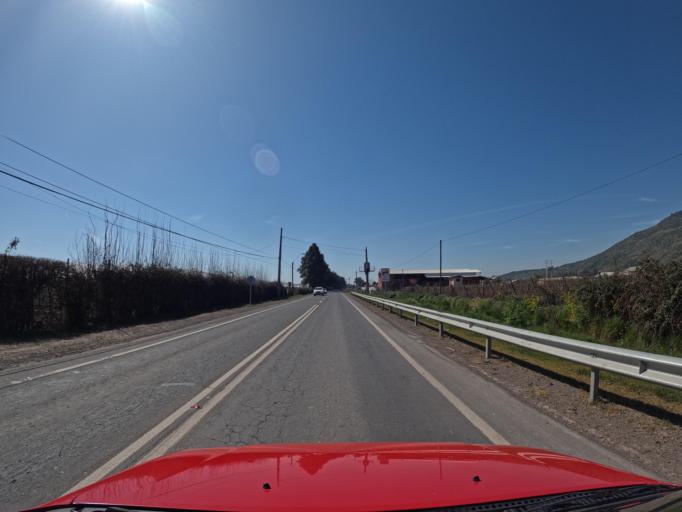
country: CL
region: Maule
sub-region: Provincia de Curico
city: Rauco
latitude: -35.0098
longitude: -71.4139
